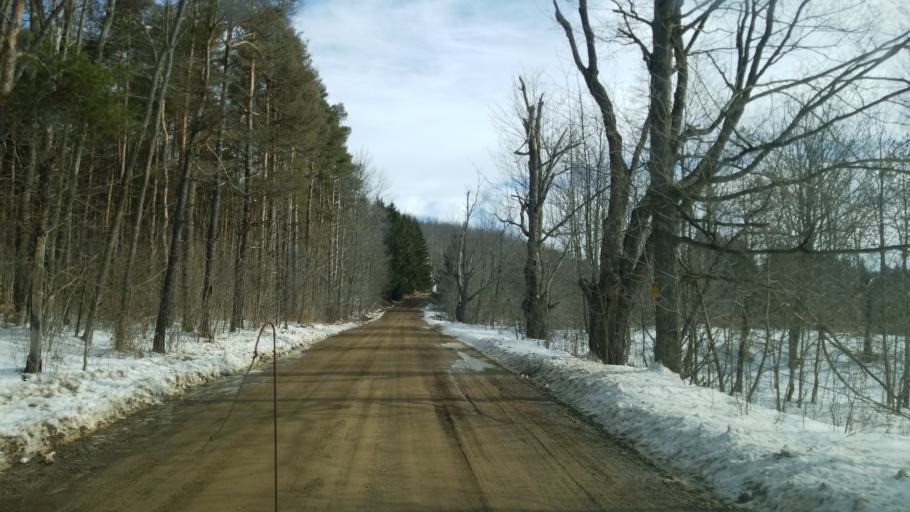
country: US
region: New York
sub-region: Allegany County
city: Andover
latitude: 42.0101
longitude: -77.8107
